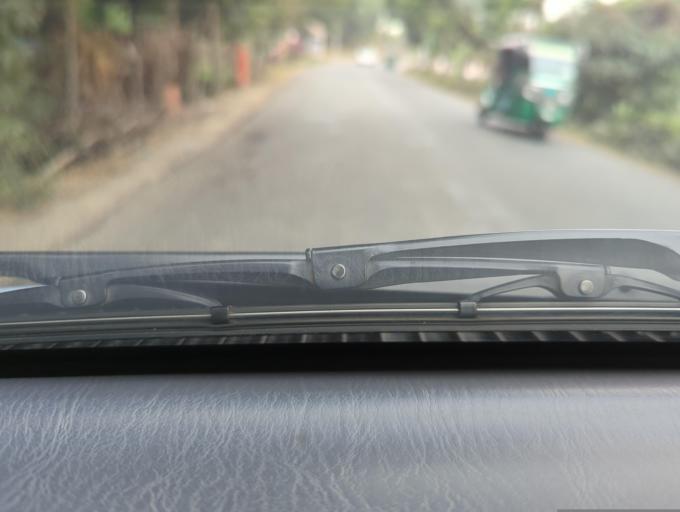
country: BD
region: Sylhet
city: Maulavi Bazar
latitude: 24.5095
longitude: 91.7272
